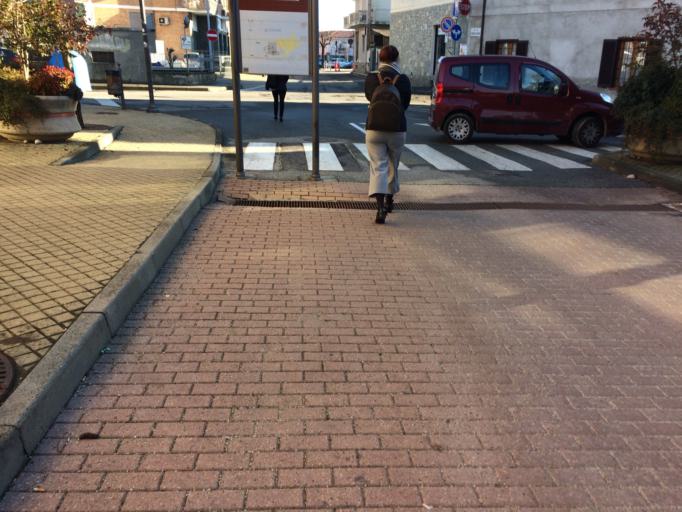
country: IT
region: Piedmont
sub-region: Provincia di Torino
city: Candiolo
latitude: 44.9604
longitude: 7.5999
